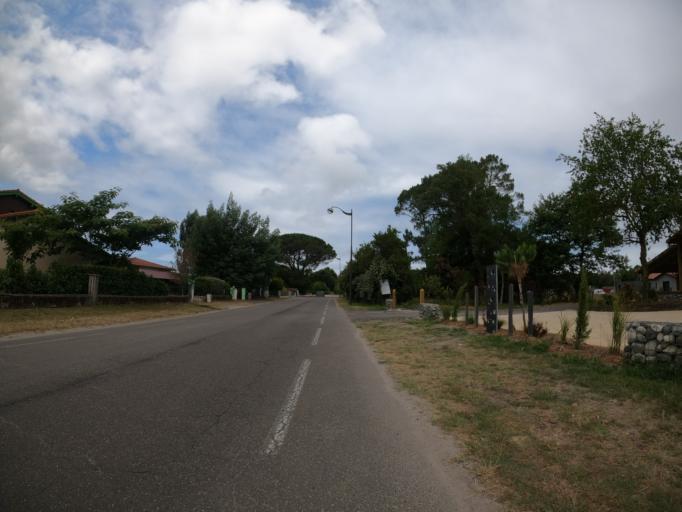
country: FR
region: Aquitaine
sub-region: Departement des Landes
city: Leon
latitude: 43.8829
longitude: -1.3097
